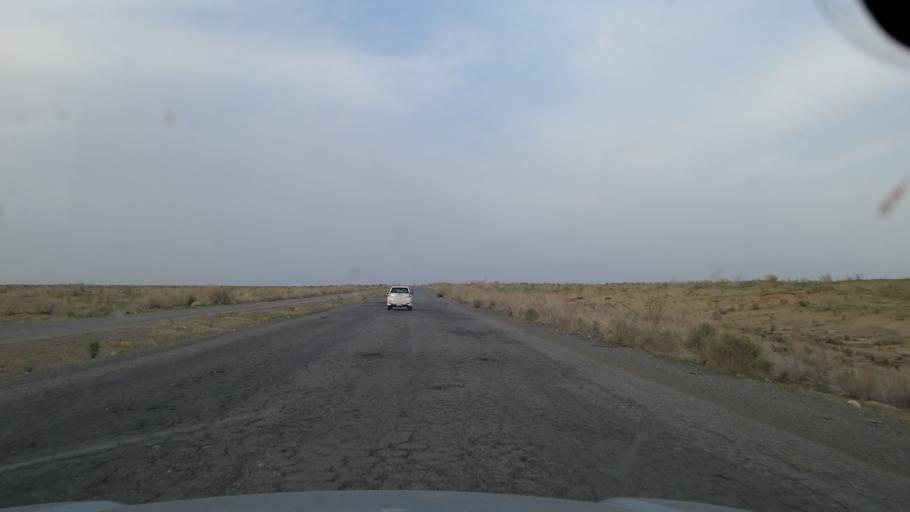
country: TM
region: Mary
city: Bayramaly
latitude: 38.2715
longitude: 62.9490
